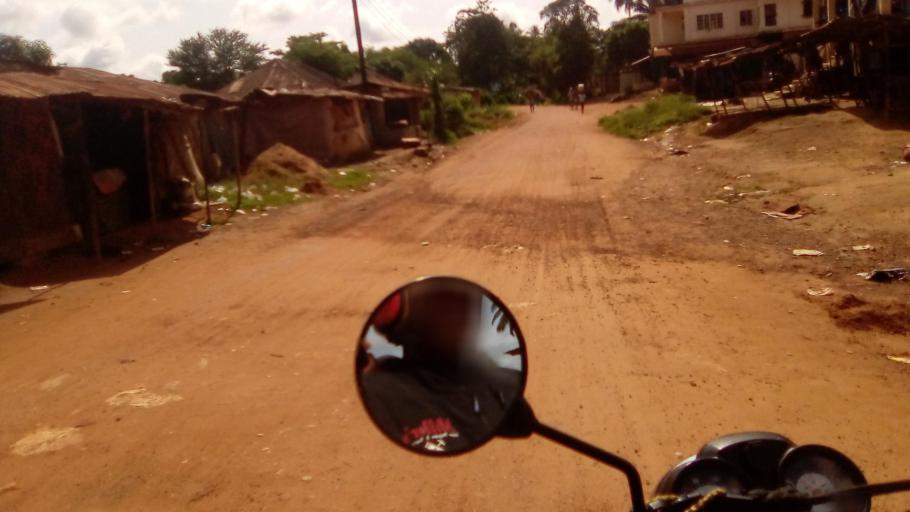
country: SL
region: Southern Province
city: Bo
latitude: 7.9595
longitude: -11.7473
